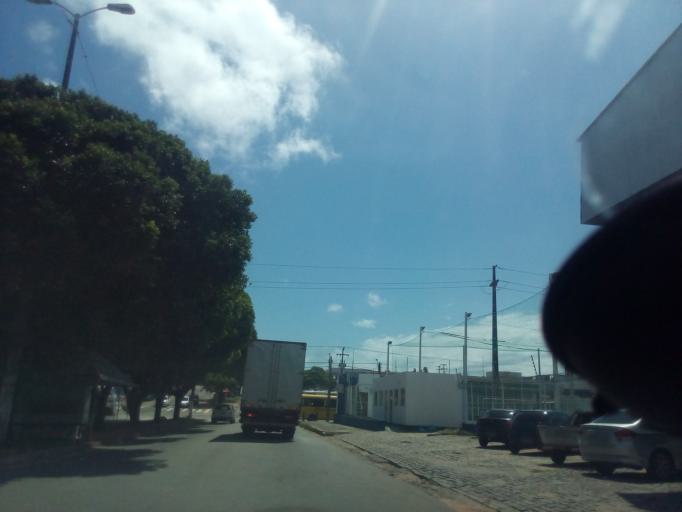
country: BR
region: Rio Grande do Norte
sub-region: Natal
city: Natal
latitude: -5.8220
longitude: -35.2330
